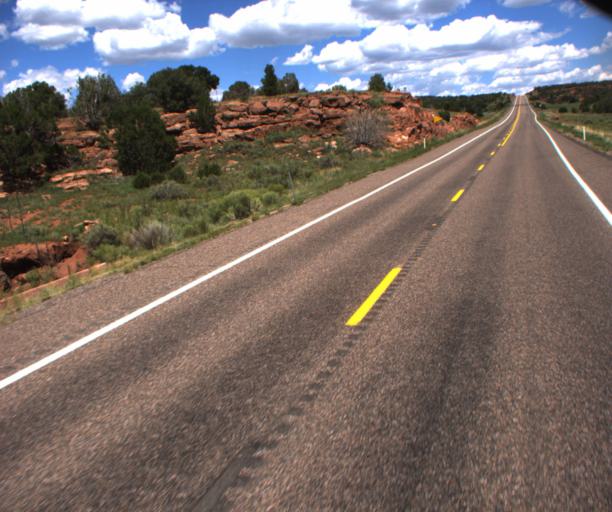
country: US
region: Arizona
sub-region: Apache County
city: Springerville
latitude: 34.1567
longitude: -109.1194
